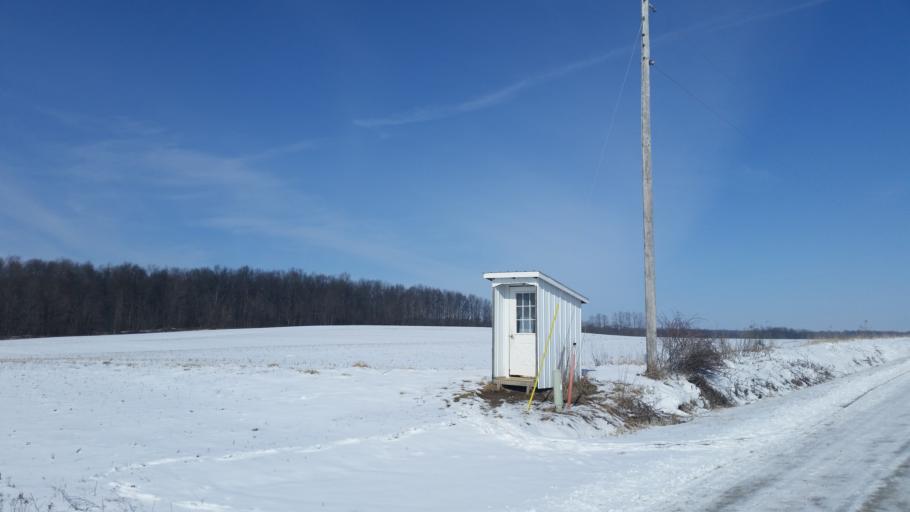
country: US
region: Ohio
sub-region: Knox County
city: Fredericktown
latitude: 40.5499
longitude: -82.6428
